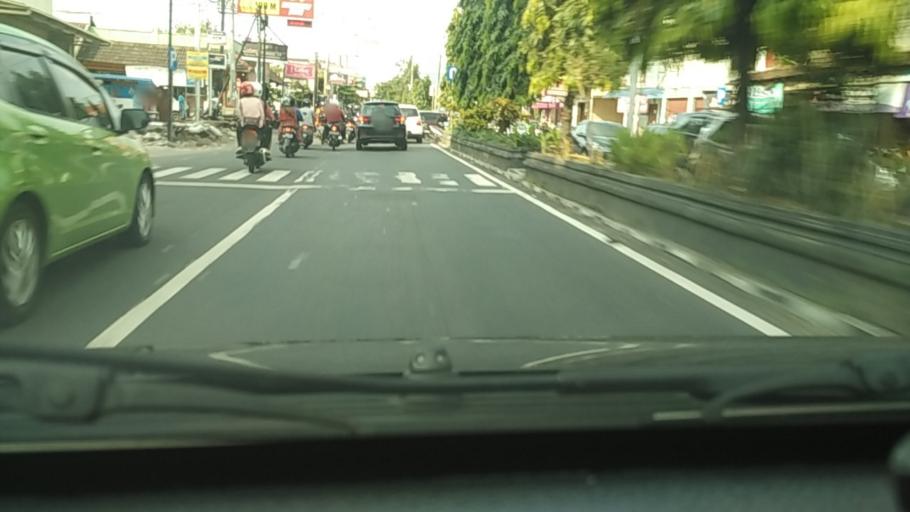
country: ID
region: Daerah Istimewa Yogyakarta
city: Yogyakarta
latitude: -7.7707
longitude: 110.3901
